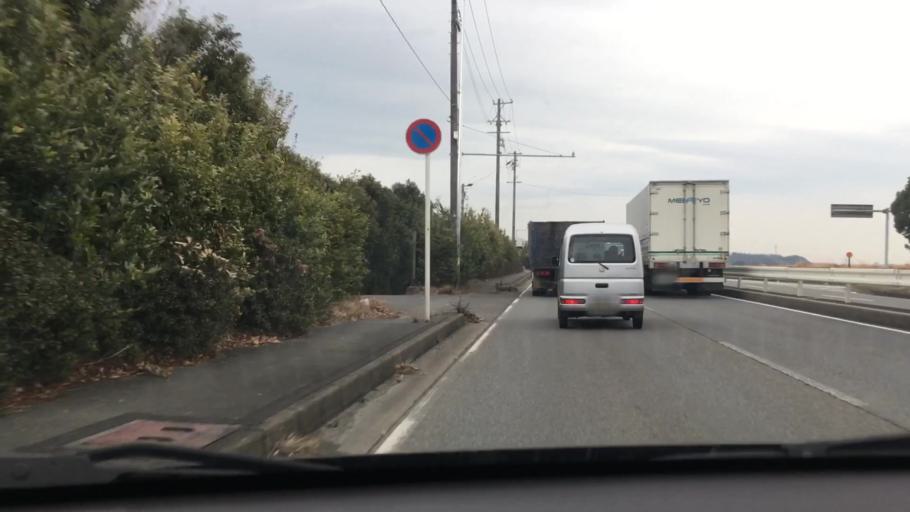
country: JP
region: Mie
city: Suzuka
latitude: 34.8839
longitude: 136.5267
